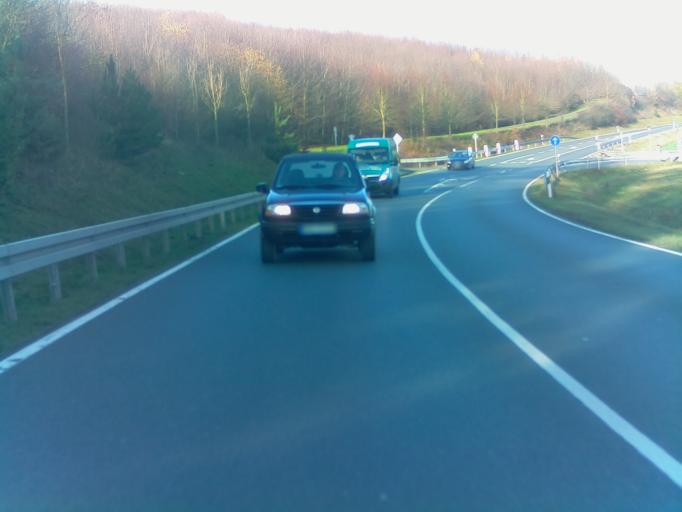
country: DE
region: Bavaria
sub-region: Regierungsbezirk Unterfranken
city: Marktheidenfeld
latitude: 49.8454
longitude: 9.5877
